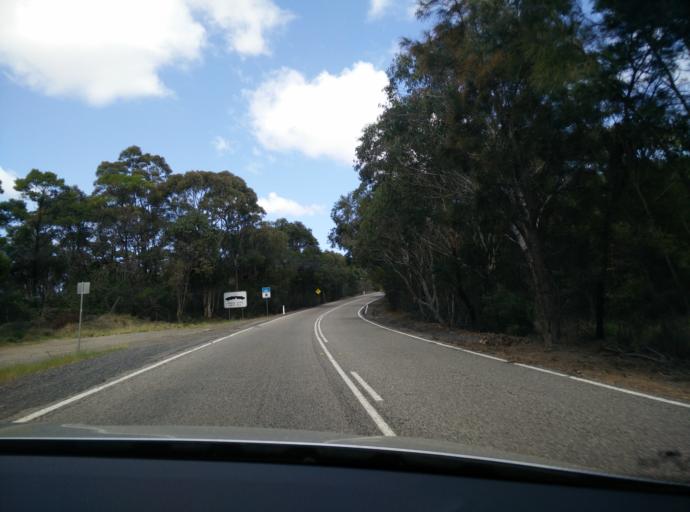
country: AU
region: New South Wales
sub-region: Gosford Shire
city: Point Clare
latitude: -33.4523
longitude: 151.2912
